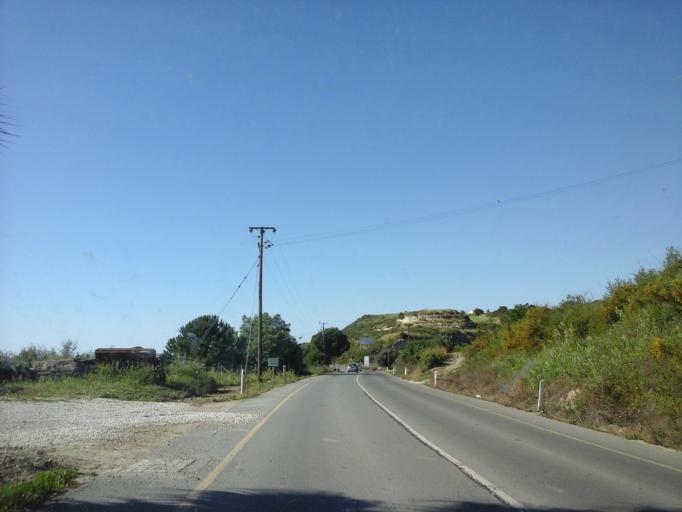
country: CY
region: Pafos
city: Polis
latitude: 34.9884
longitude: 32.4512
